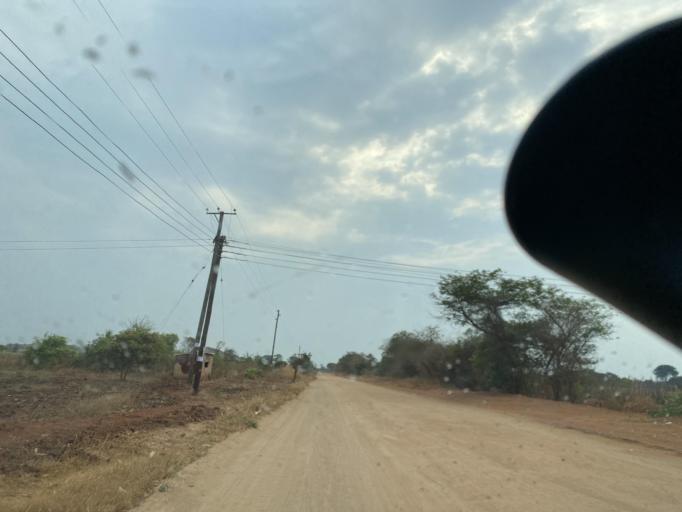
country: ZM
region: Lusaka
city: Lusaka
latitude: -15.2891
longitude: 28.2839
